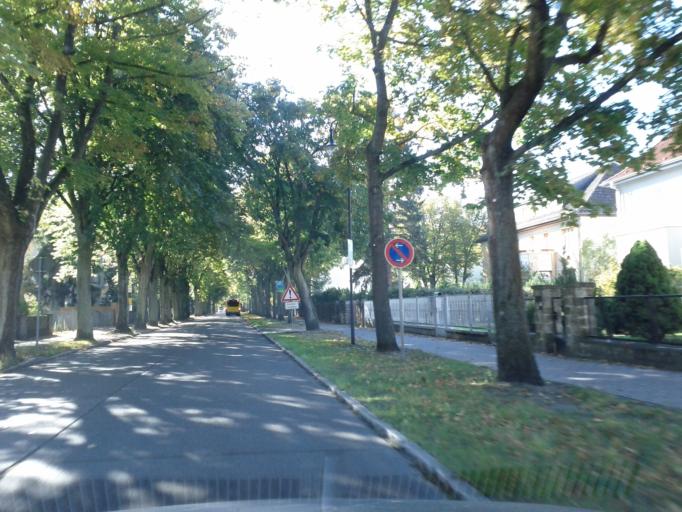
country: DE
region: Brandenburg
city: Schoneiche
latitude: 52.4623
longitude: 13.6991
